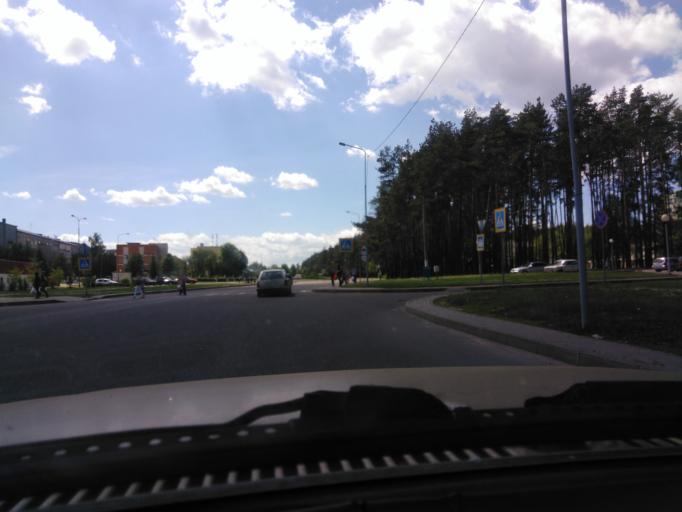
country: BY
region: Mogilev
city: Mahilyow
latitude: 53.9171
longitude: 30.2815
